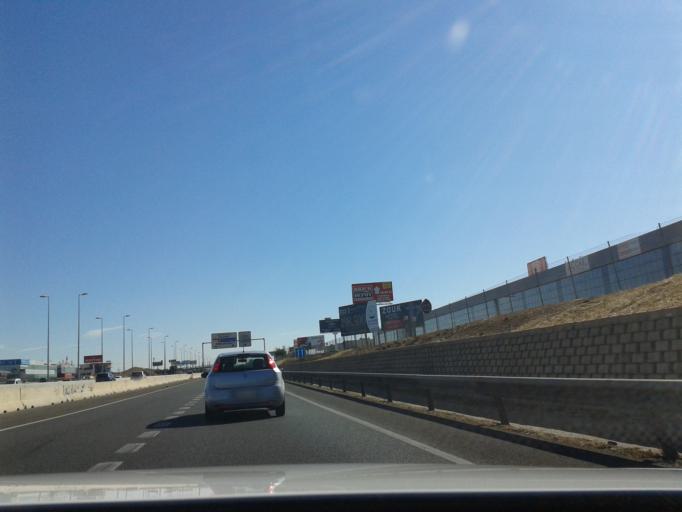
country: ES
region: Madrid
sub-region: Provincia de Madrid
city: Alcala de Henares
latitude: 40.4879
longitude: -3.3946
